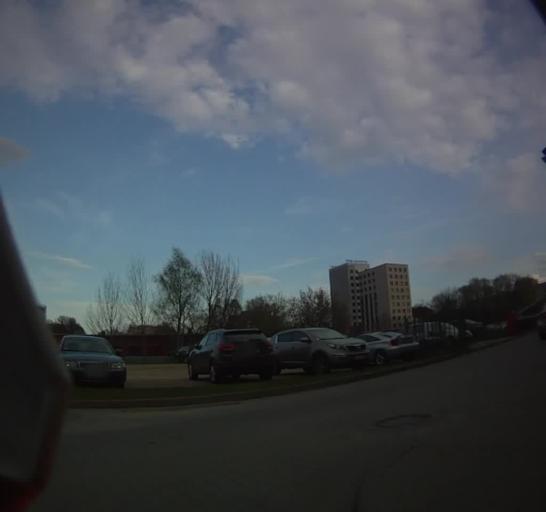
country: LV
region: Riga
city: Riga
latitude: 56.9765
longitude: 24.1321
